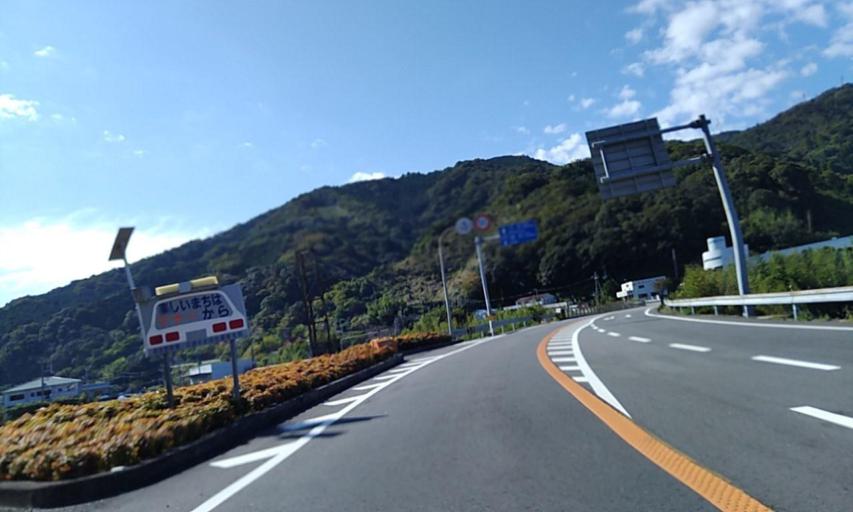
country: JP
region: Wakayama
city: Gobo
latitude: 34.0033
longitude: 135.1915
